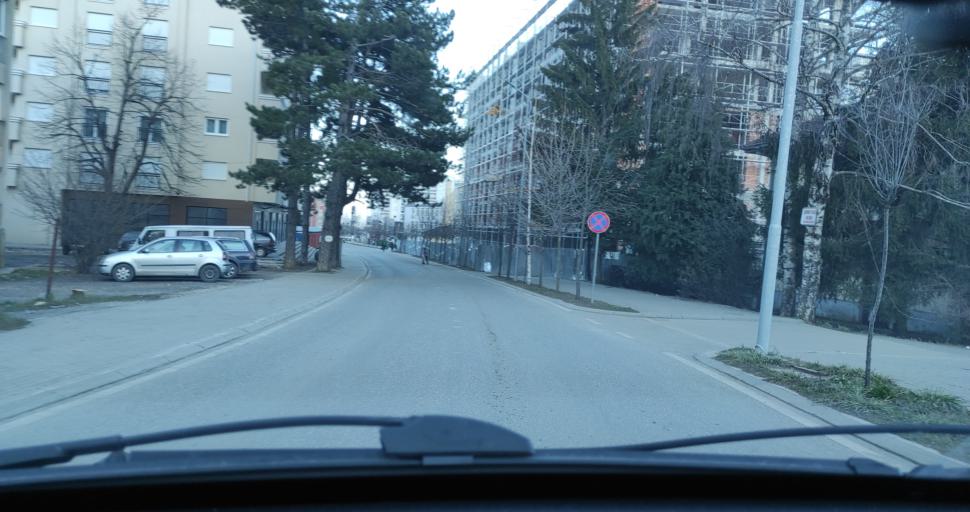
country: XK
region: Gjakova
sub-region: Komuna e Decanit
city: Decan
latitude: 42.5396
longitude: 20.2854
